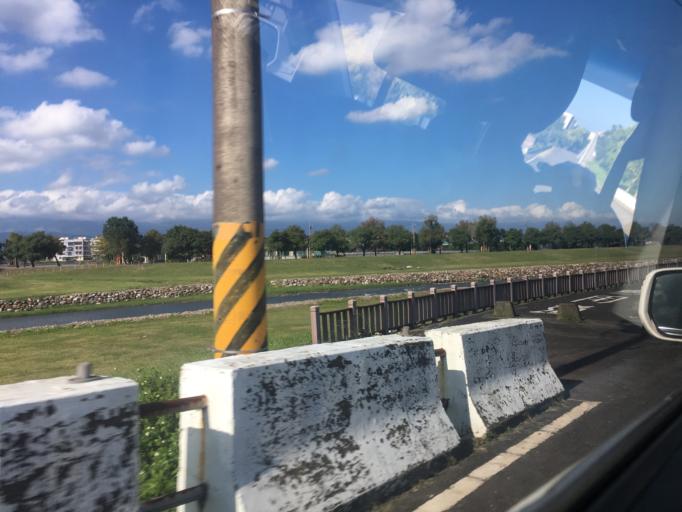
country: TW
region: Taiwan
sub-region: Yilan
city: Yilan
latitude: 24.6920
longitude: 121.7405
